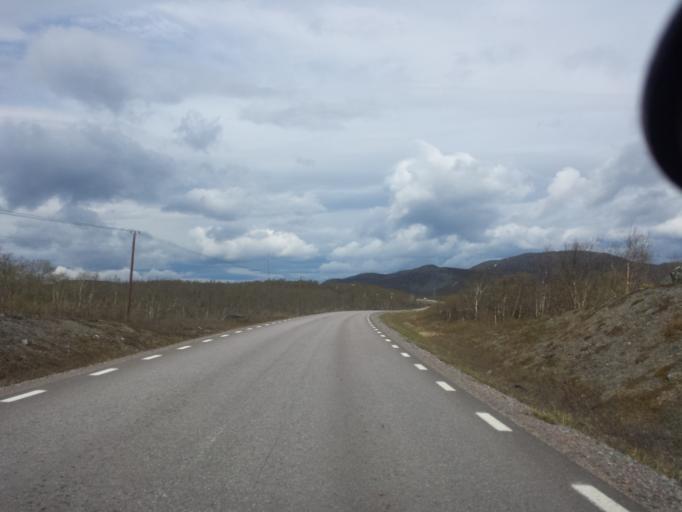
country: SE
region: Norrbotten
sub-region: Kiruna Kommun
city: Kiruna
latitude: 68.1666
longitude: 19.7874
